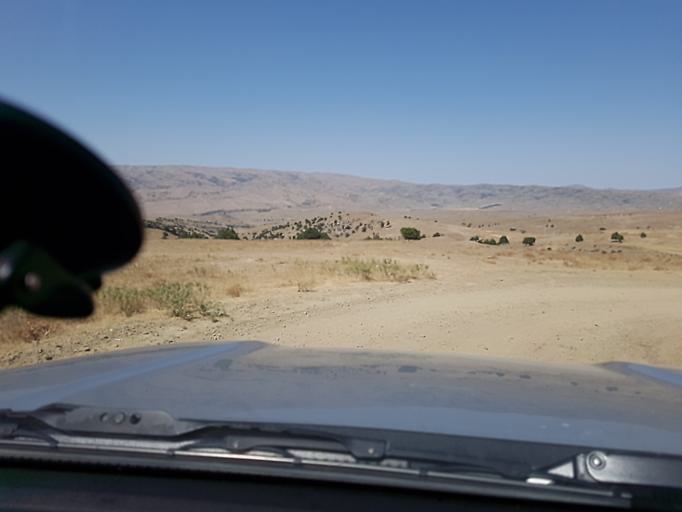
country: TM
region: Ahal
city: Baharly
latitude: 38.3644
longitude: 56.8840
